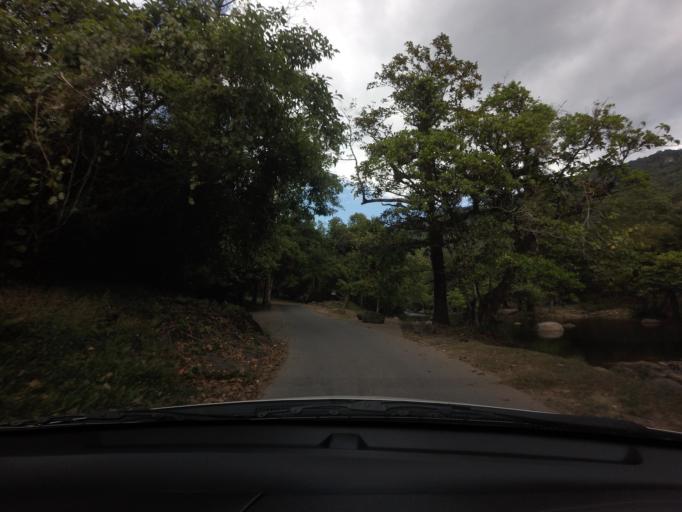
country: TH
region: Nakhon Nayok
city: Nakhon Nayok
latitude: 14.3315
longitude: 101.3048
